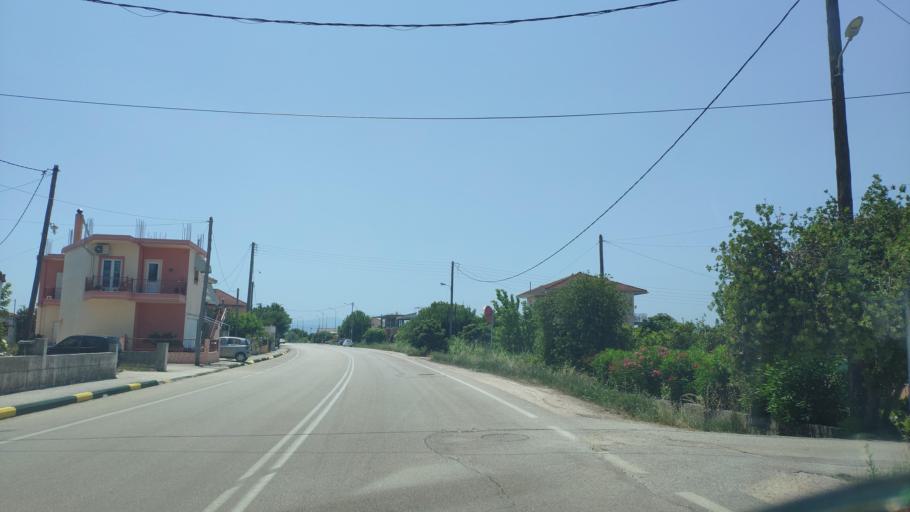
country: GR
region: Epirus
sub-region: Nomos Artas
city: Kostakioi
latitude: 39.1315
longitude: 20.9837
